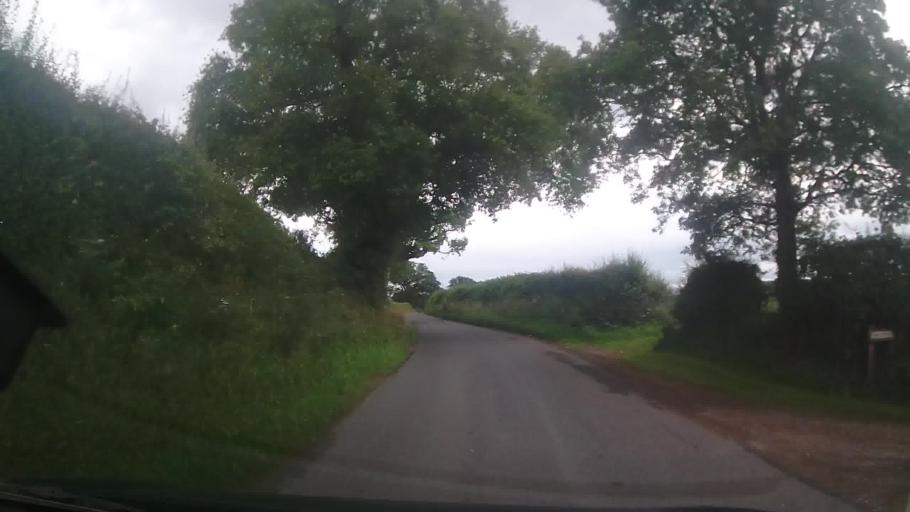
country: GB
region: England
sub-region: Shropshire
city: Whitchurch
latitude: 52.9394
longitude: -2.7304
